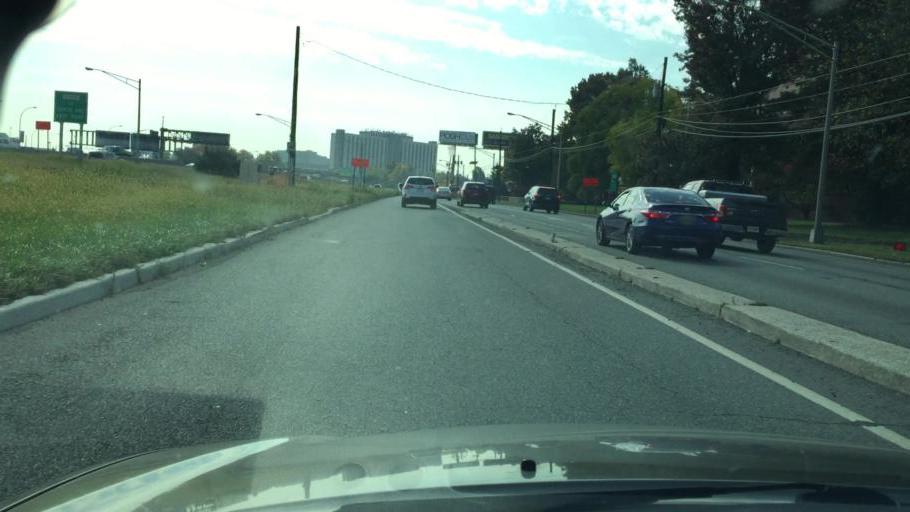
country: US
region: New Jersey
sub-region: Union County
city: Elizabeth
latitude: 40.6925
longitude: -74.1905
